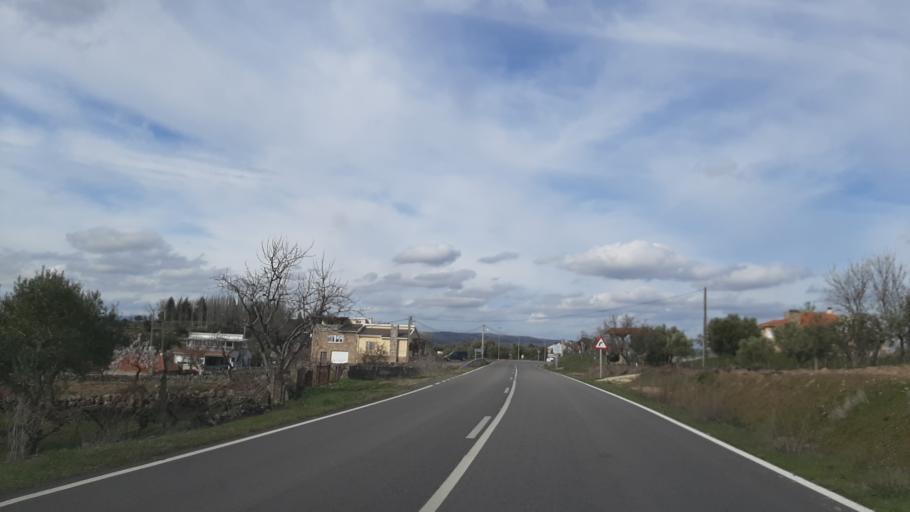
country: ES
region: Castille and Leon
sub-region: Provincia de Salamanca
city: Villarino de los Aires
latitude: 41.2620
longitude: -6.4716
